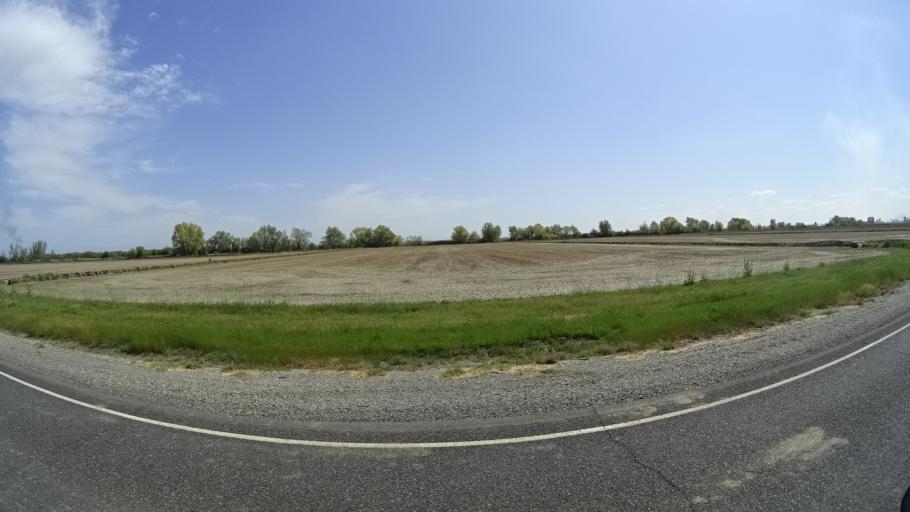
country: US
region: California
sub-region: Butte County
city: Durham
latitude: 39.4753
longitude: -121.9303
